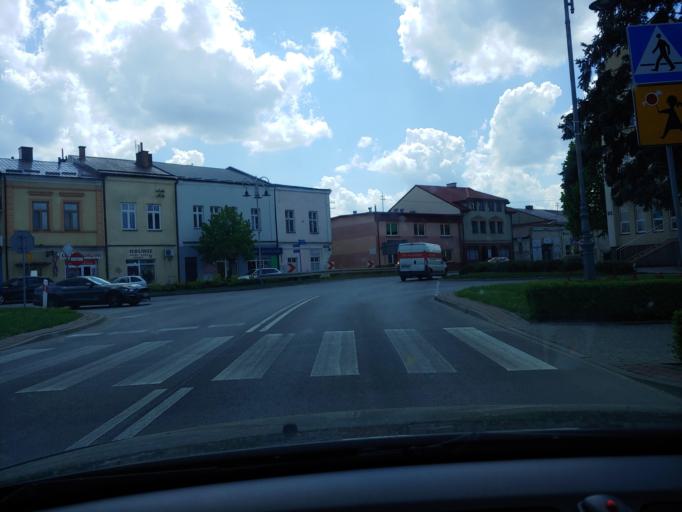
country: PL
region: Subcarpathian Voivodeship
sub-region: Powiat mielecki
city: Radomysl Wielki
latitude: 50.1960
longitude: 21.2767
